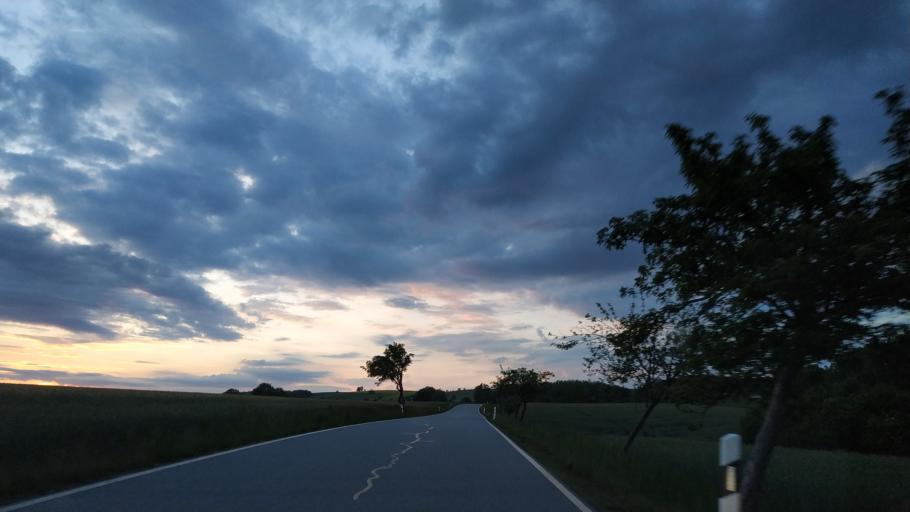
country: DE
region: Saxony
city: Hohnstein
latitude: 50.9779
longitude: 14.0909
